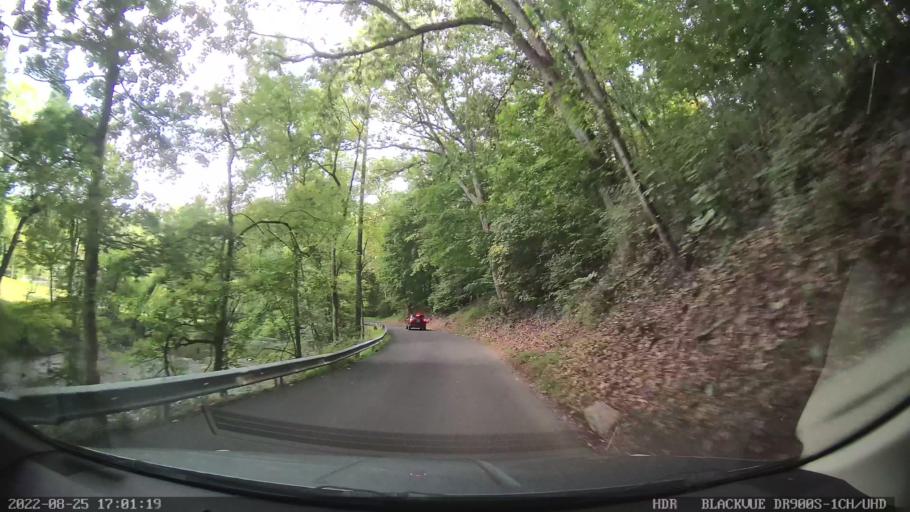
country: US
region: Pennsylvania
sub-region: Lehigh County
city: Dorneyville
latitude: 40.5576
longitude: -75.5085
